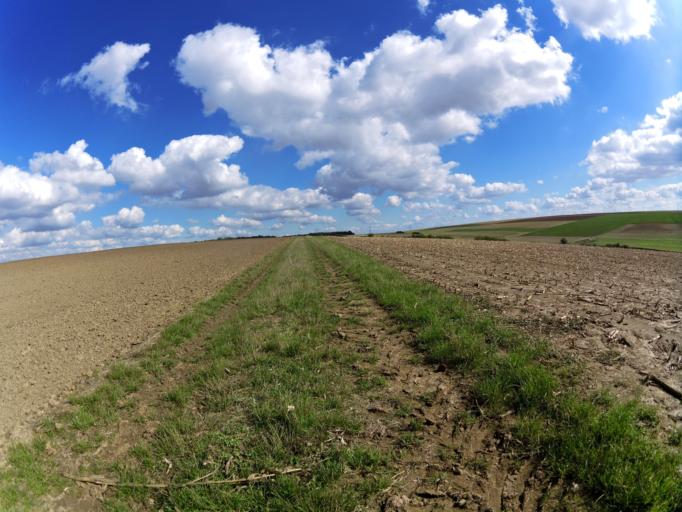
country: DE
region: Bavaria
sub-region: Regierungsbezirk Unterfranken
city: Frickenhausen
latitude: 49.6905
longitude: 10.0895
